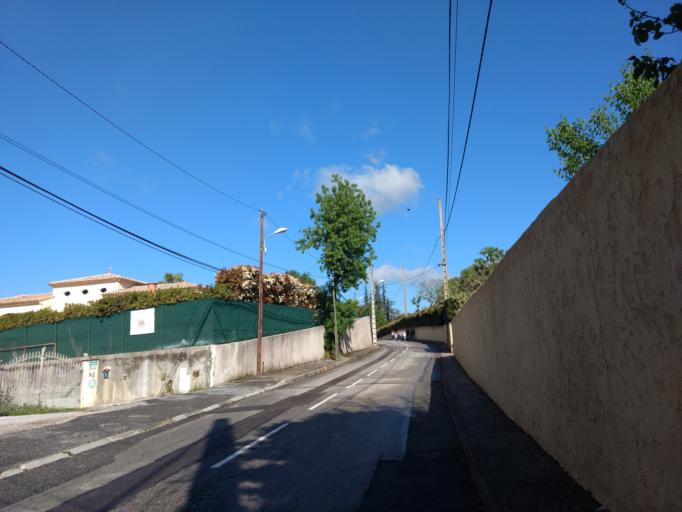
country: FR
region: Provence-Alpes-Cote d'Azur
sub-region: Departement des Alpes-Maritimes
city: Biot
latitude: 43.6189
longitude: 7.1271
